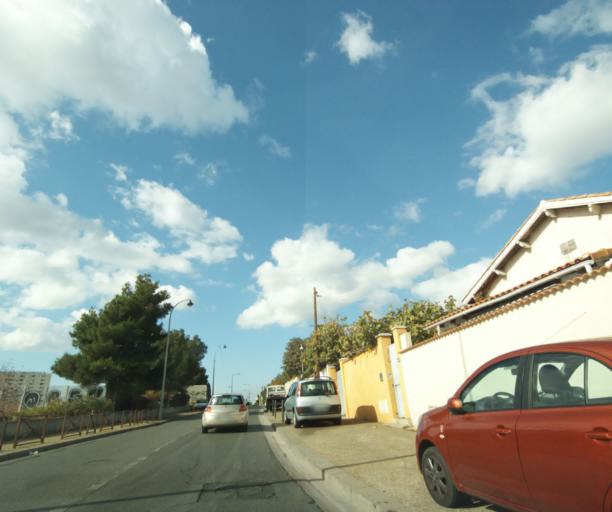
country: FR
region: Provence-Alpes-Cote d'Azur
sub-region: Departement des Bouches-du-Rhone
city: Marseille 13
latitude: 43.3291
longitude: 5.4156
